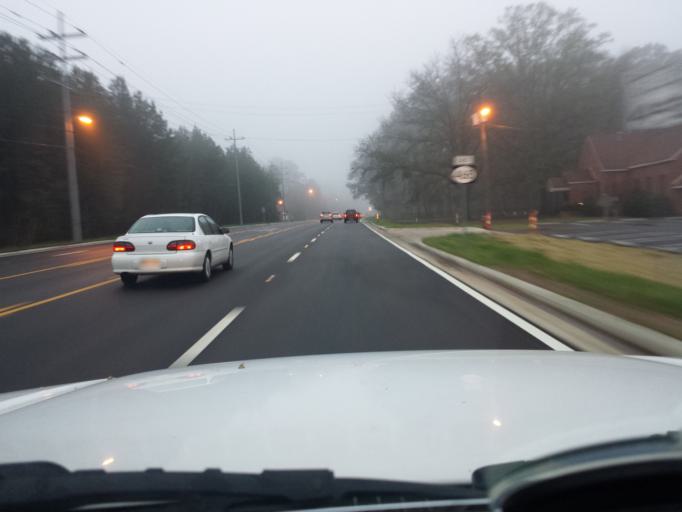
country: US
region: Mississippi
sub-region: Rankin County
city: Flowood
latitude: 32.3289
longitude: -90.0924
